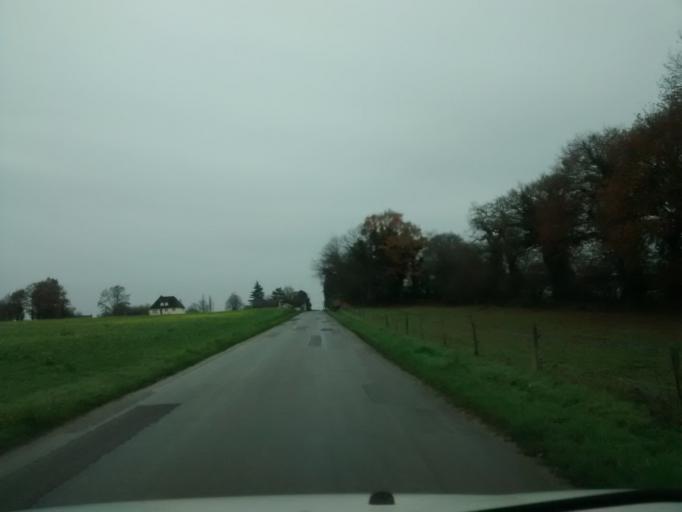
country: FR
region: Brittany
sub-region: Departement d'Ille-et-Vilaine
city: Acigne
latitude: 48.1418
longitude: -1.5476
